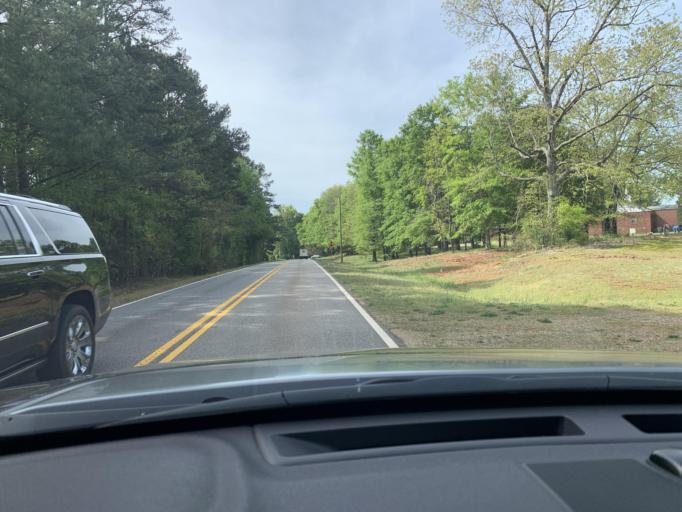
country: US
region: Georgia
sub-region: Oconee County
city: Watkinsville
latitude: 33.8290
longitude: -83.5065
